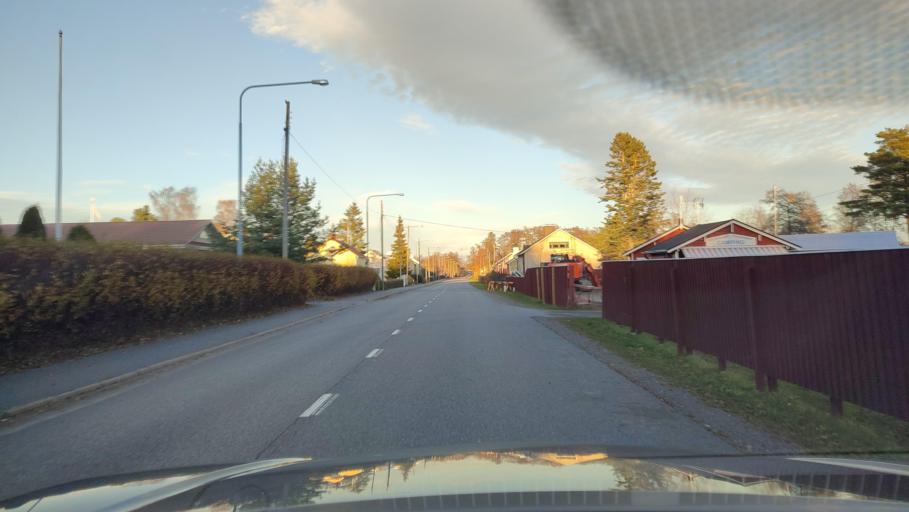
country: FI
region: Ostrobothnia
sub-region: Sydosterbotten
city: Kristinestad
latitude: 62.2644
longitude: 21.3621
